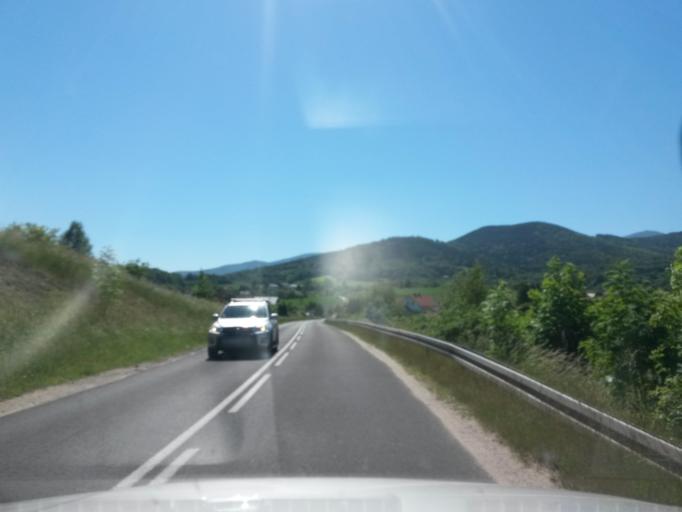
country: PL
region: Lower Silesian Voivodeship
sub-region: Powiat jeleniogorski
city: Sosnowka
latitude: 50.8277
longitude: 15.7224
